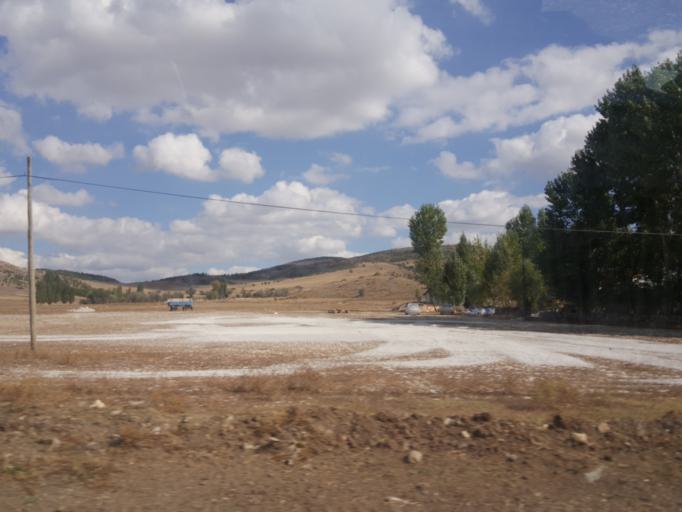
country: TR
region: Tokat
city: Artova
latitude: 40.1071
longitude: 36.3035
